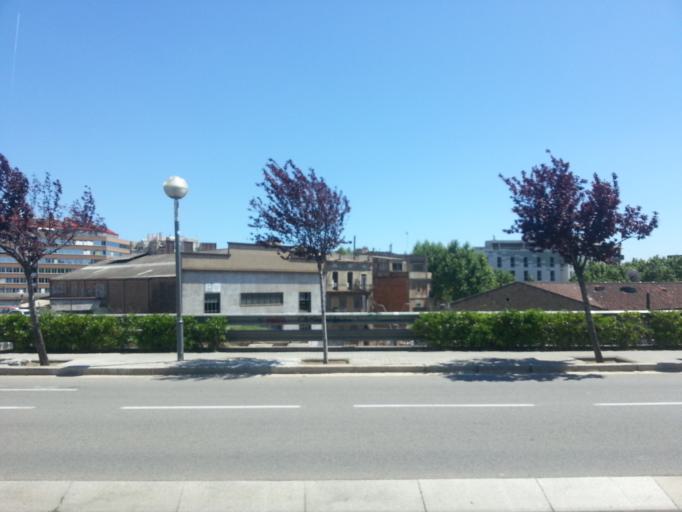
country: ES
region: Catalonia
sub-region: Provincia de Barcelona
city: Sant Marti
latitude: 41.3993
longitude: 2.1870
